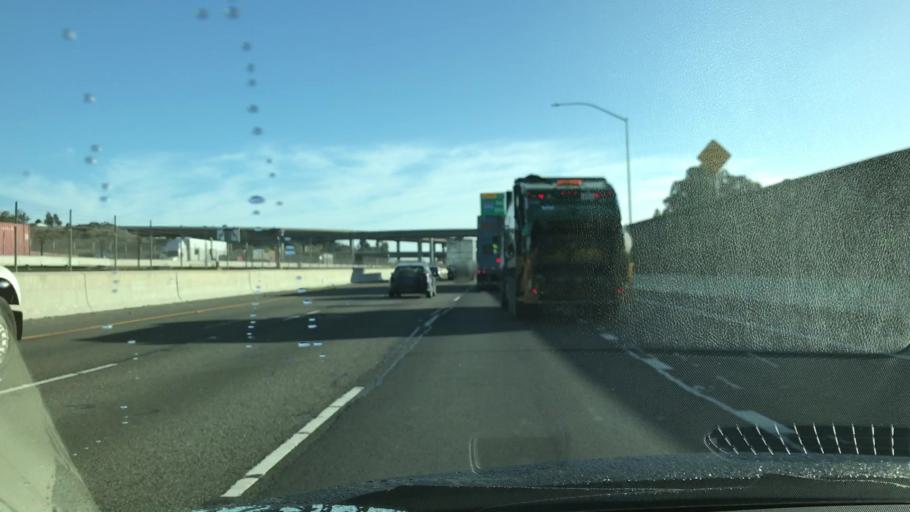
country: US
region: California
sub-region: Alameda County
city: Cherryland
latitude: 37.6892
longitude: -122.1041
